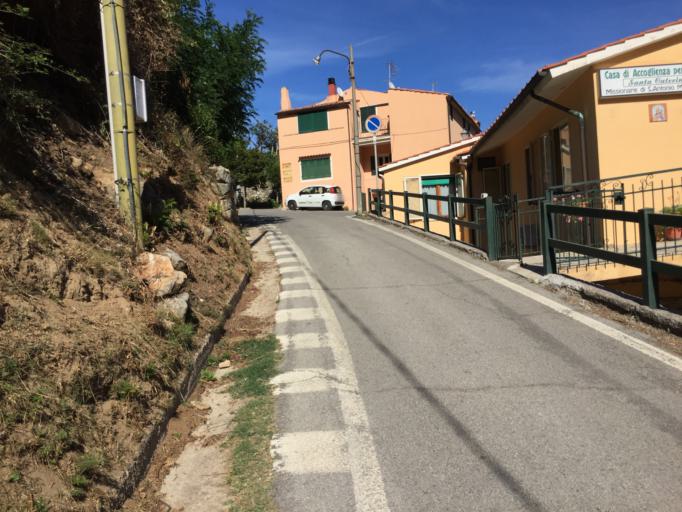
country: IT
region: Tuscany
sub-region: Provincia di Livorno
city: Marciana
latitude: 42.7877
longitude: 10.1671
